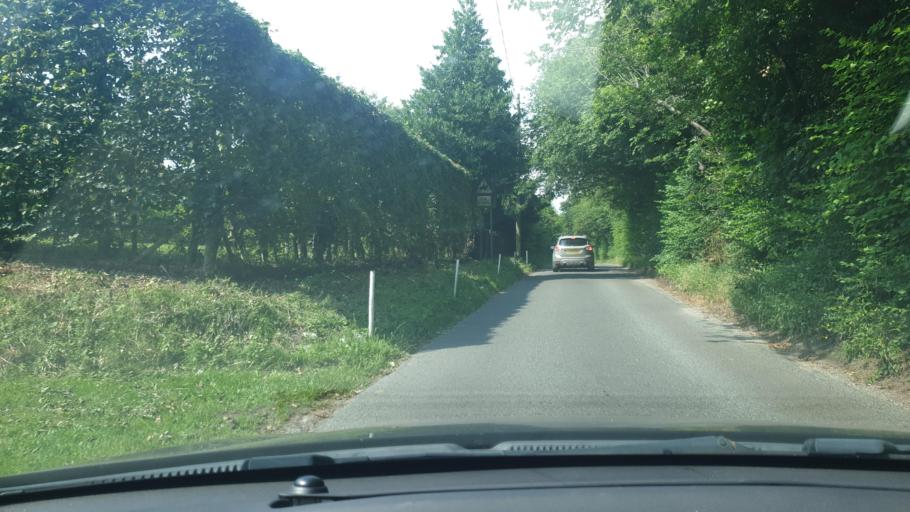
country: GB
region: England
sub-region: Essex
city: Manningtree
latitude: 51.9405
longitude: 1.0314
